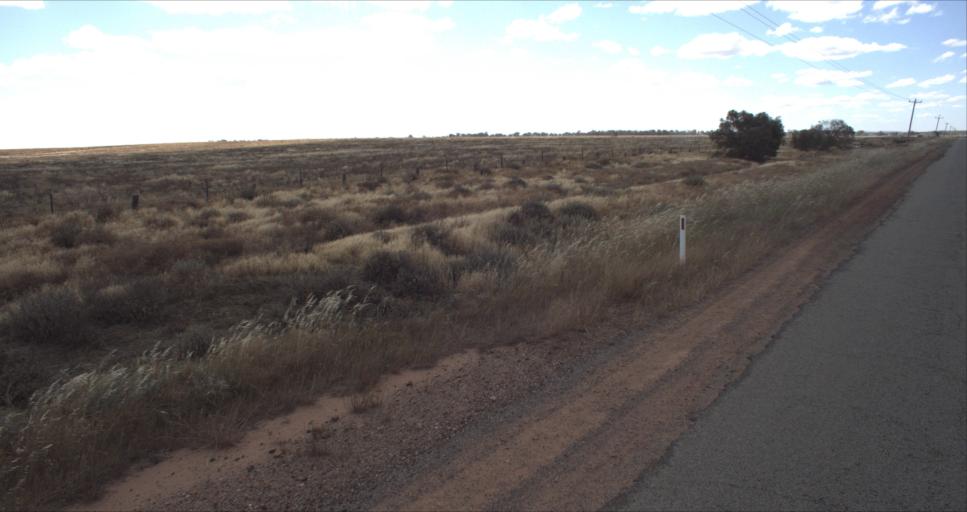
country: AU
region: New South Wales
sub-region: Leeton
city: Leeton
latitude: -34.4813
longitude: 146.2490
